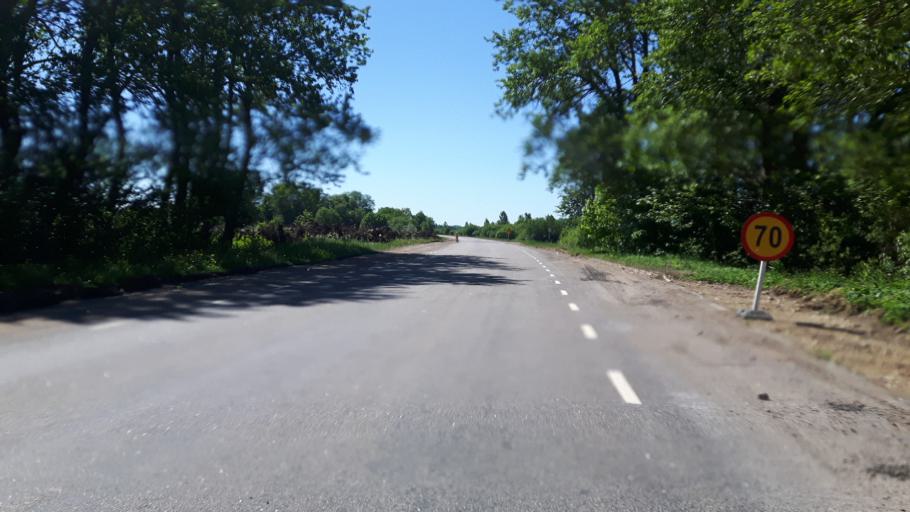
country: EE
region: Ida-Virumaa
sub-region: Narva-Joesuu linn
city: Narva-Joesuu
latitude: 59.3920
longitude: 27.9227
